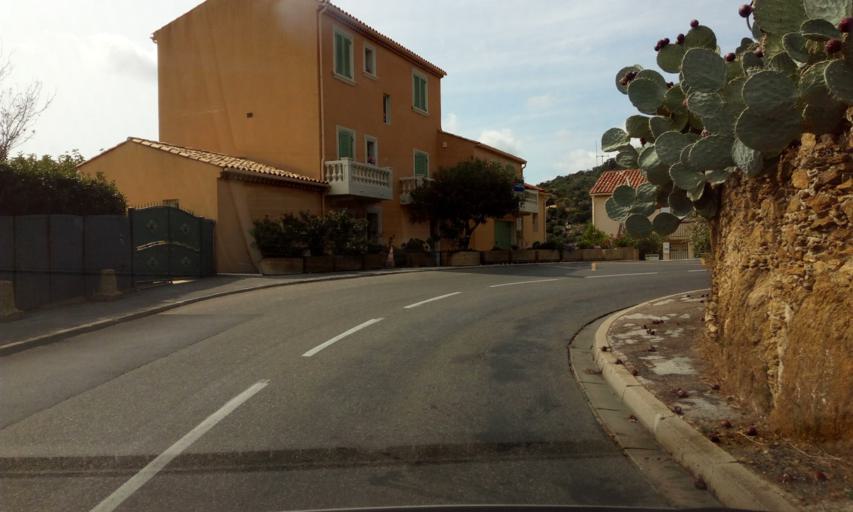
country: FR
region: Provence-Alpes-Cote d'Azur
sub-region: Departement du Var
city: Bormes-les-Mimosas
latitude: 43.1491
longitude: 6.3425
